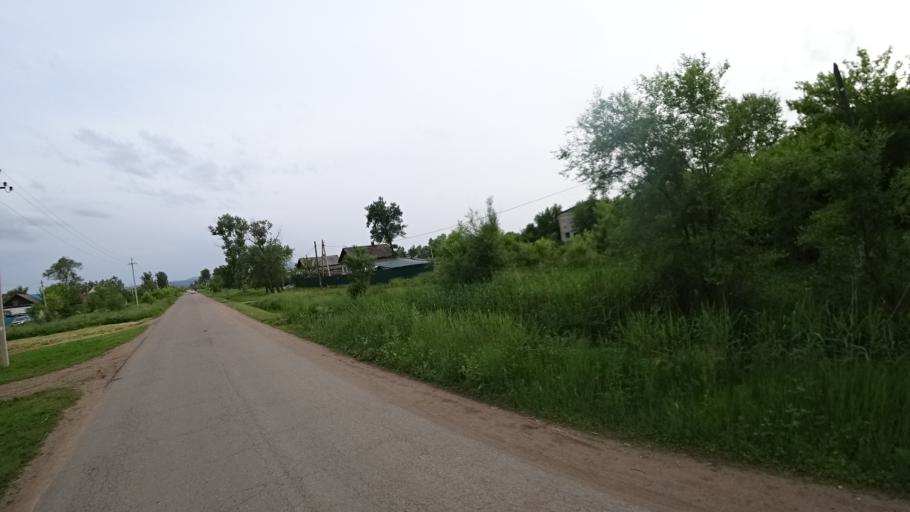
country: RU
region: Primorskiy
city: Novosysoyevka
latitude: 44.2428
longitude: 133.3676
